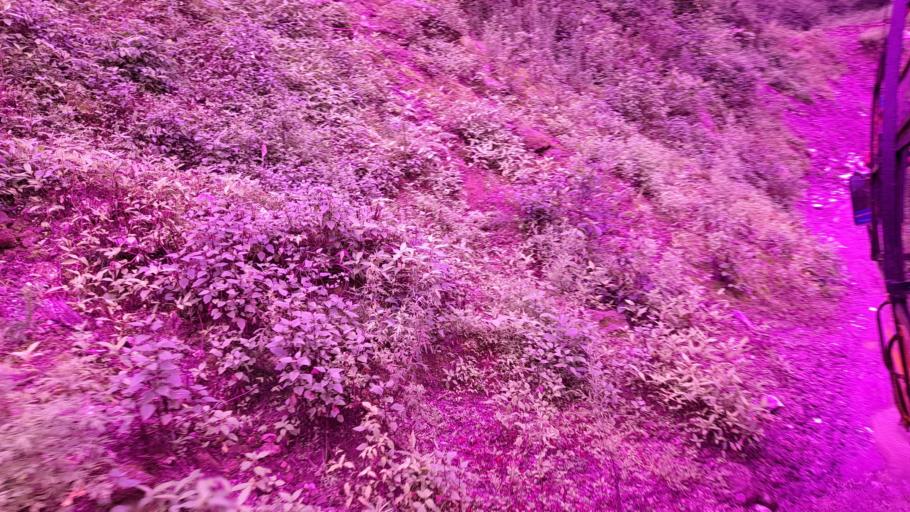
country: NP
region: Central Region
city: Kirtipur
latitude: 27.8142
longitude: 85.2117
